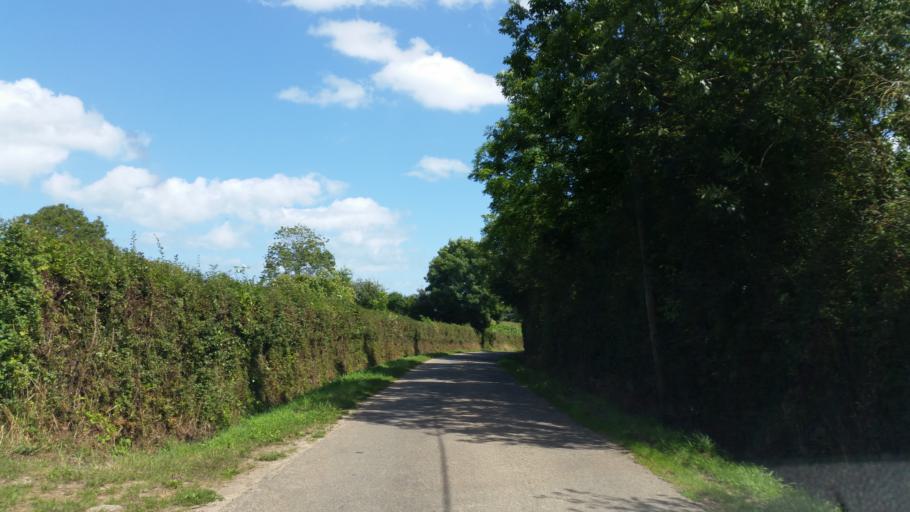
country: FR
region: Lower Normandy
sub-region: Departement de la Manche
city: Sainte-Mere-Eglise
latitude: 49.4593
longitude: -1.3239
